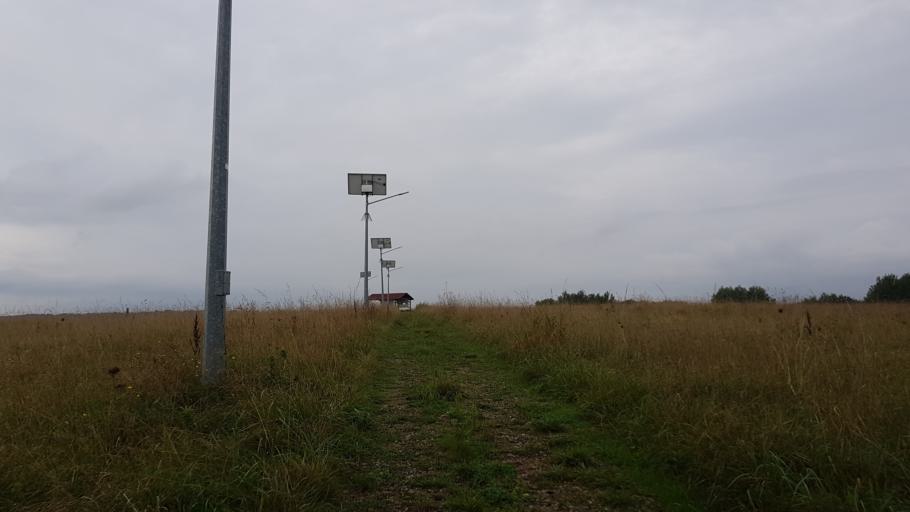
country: PL
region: West Pomeranian Voivodeship
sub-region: Powiat gryficki
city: Trzebiatow
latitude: 54.0736
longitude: 15.2110
